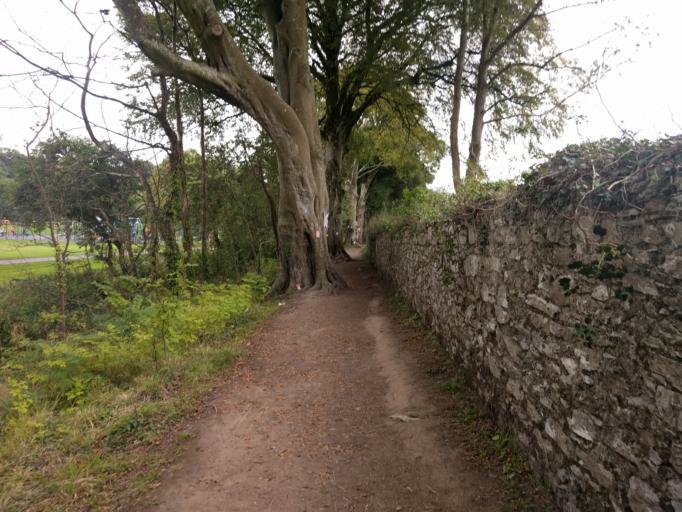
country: IE
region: Munster
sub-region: County Cork
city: Tower
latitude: 51.8909
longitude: -8.6173
